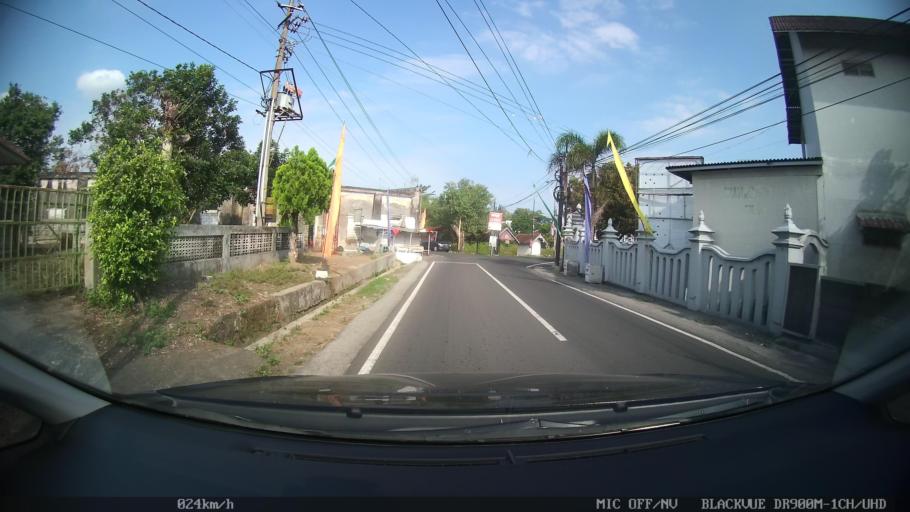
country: ID
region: Central Java
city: Candi Prambanan
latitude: -7.7319
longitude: 110.4604
